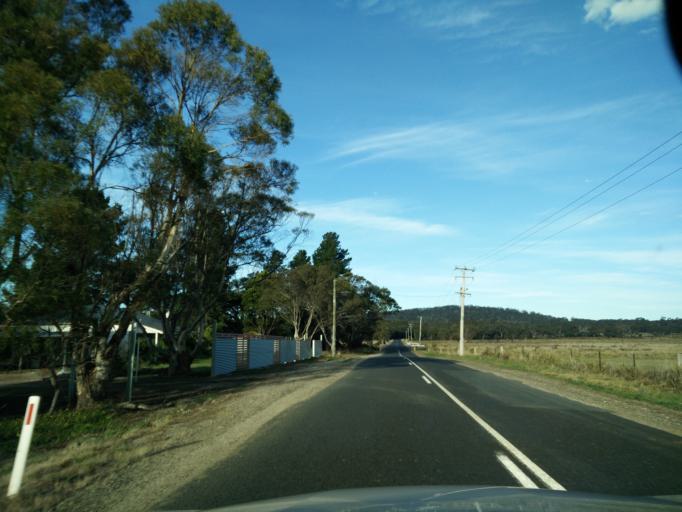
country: AU
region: Tasmania
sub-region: Break O'Day
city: St Helens
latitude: -41.8914
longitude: 148.2669
